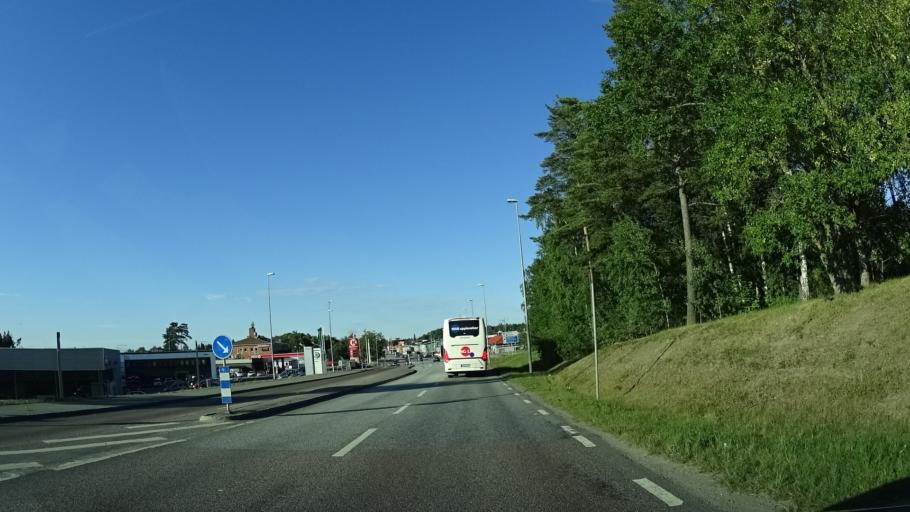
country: SE
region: Stockholm
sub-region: Norrtalje Kommun
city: Norrtalje
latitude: 59.7484
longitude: 18.6870
